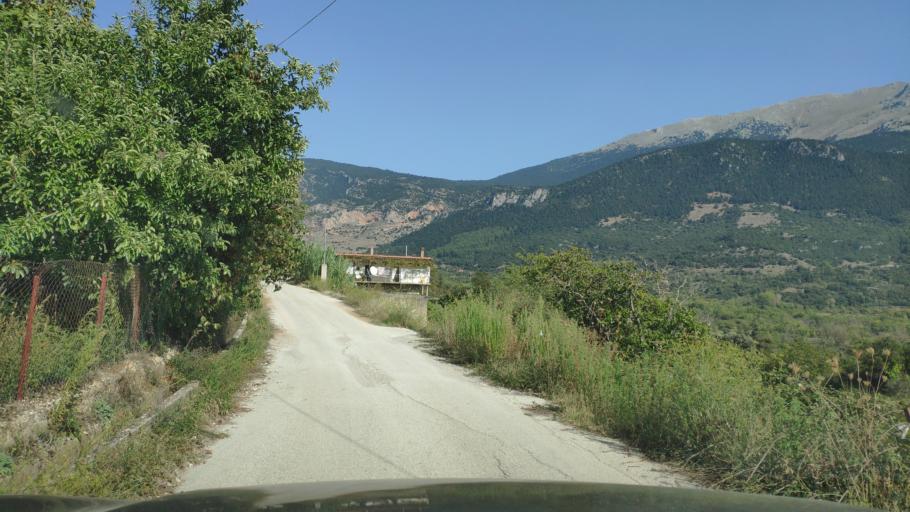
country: GR
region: West Greece
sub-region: Nomos Achaias
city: Aiyira
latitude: 37.9501
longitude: 22.3266
